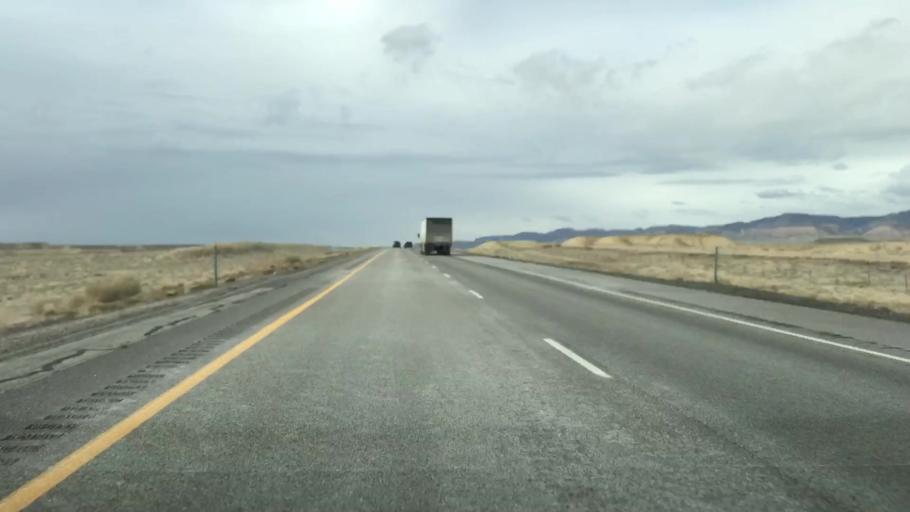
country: US
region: Utah
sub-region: Grand County
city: Moab
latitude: 38.9383
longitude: -109.4886
